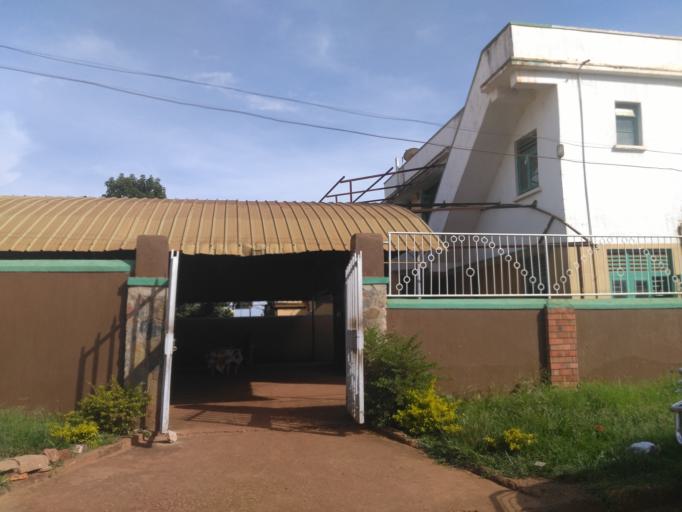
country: UG
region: Eastern Region
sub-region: Jinja District
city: Jinja
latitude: 0.4348
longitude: 33.2088
